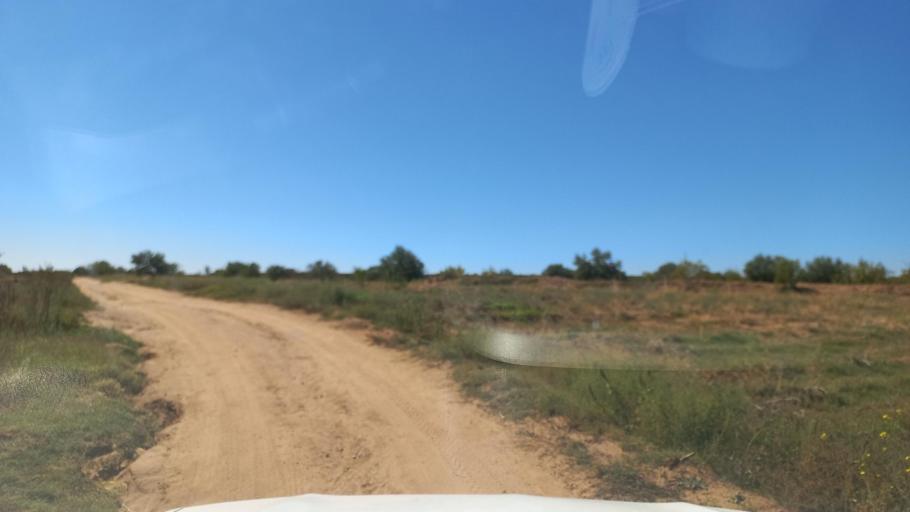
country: TN
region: Al Qasrayn
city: Sbiba
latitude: 35.3619
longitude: 9.0831
